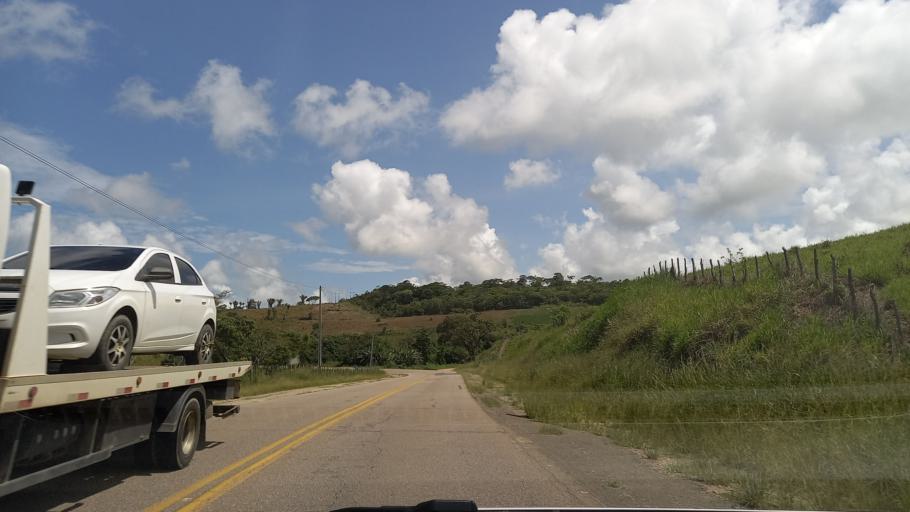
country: BR
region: Pernambuco
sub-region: Barreiros
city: Barreiros
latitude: -8.7563
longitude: -35.1713
